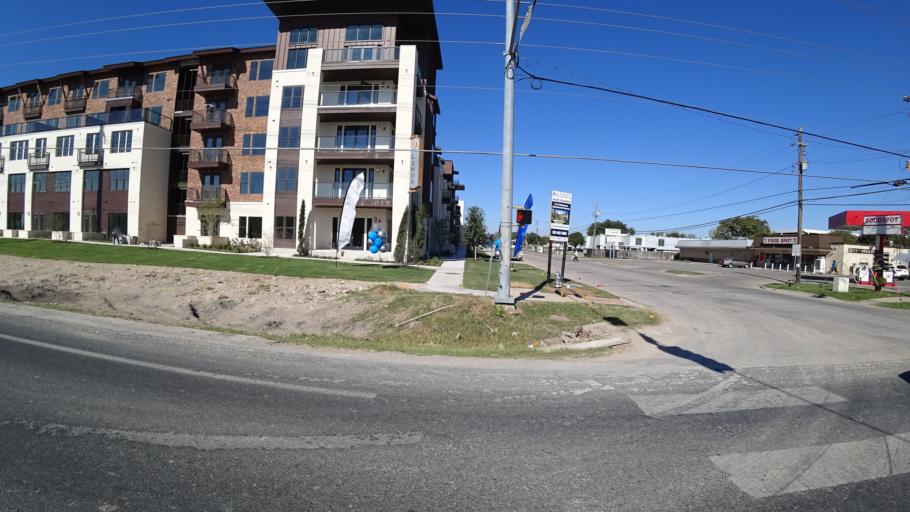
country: US
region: Texas
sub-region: Travis County
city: Austin
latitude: 30.2387
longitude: -97.7196
